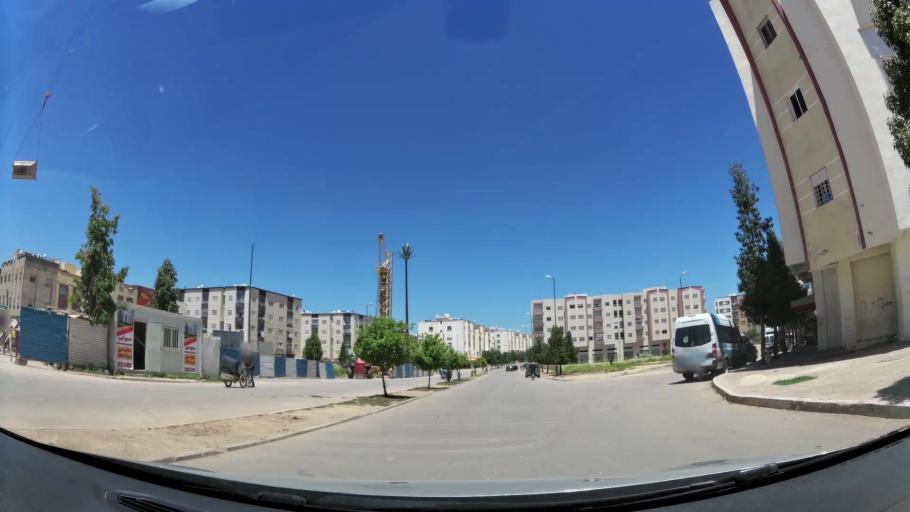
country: MA
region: Meknes-Tafilalet
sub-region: Meknes
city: Meknes
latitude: 33.8617
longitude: -5.5620
